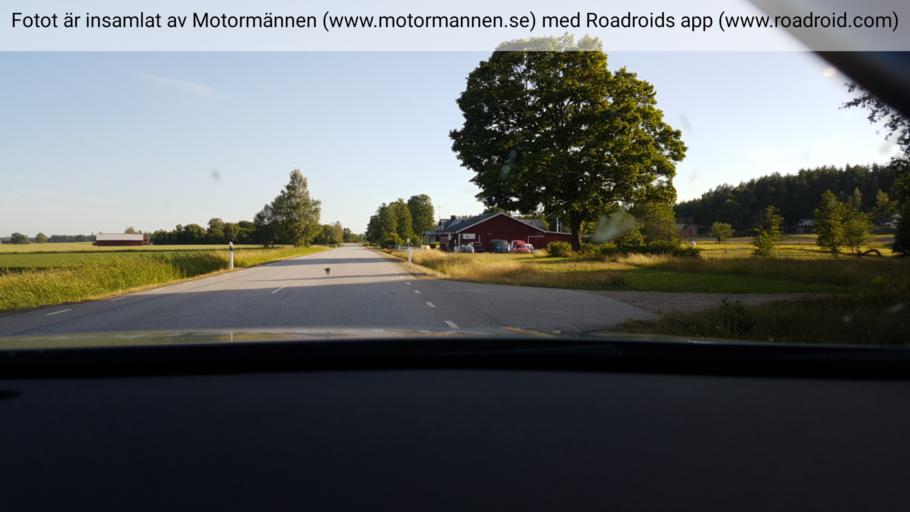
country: SE
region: Vaestra Goetaland
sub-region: Toreboda Kommun
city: Toereboda
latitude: 58.6307
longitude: 14.0187
